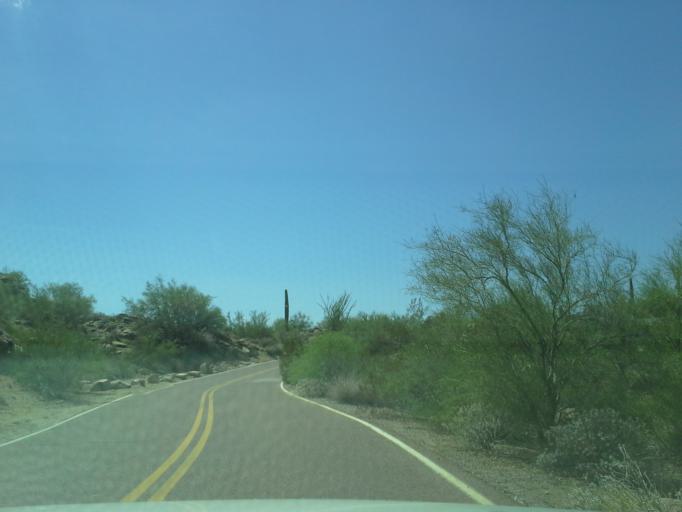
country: US
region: Arizona
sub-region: Maricopa County
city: Guadalupe
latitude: 33.3420
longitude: -112.0579
